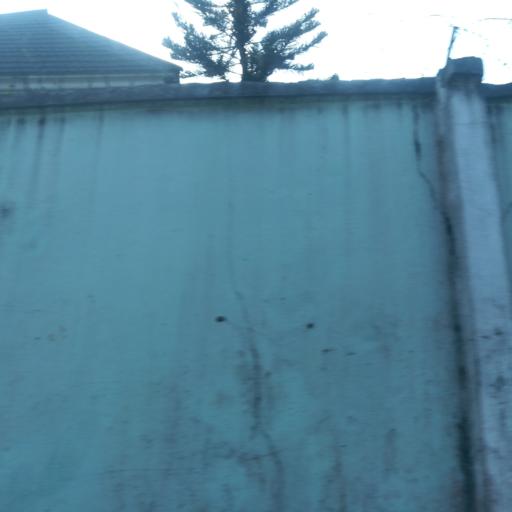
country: NG
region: Rivers
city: Port Harcourt
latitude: 4.8605
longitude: 6.9651
